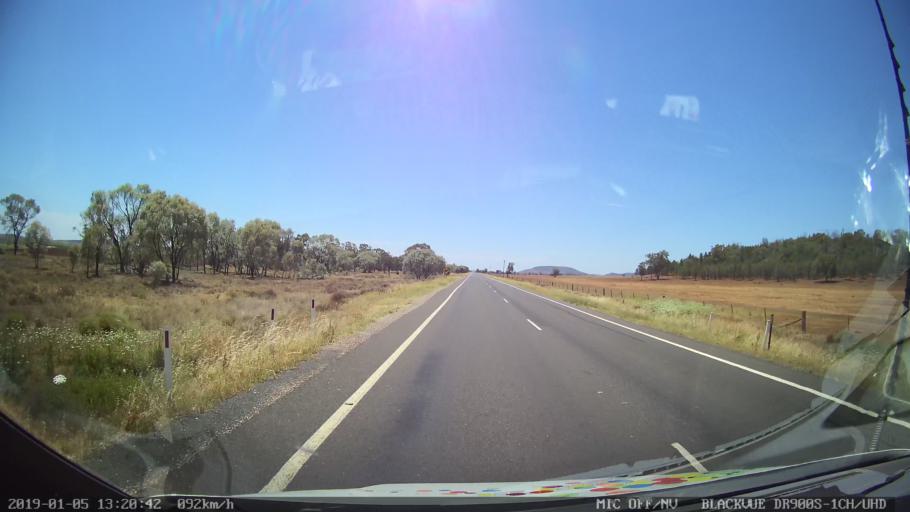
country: AU
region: New South Wales
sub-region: Gunnedah
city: Gunnedah
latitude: -31.1003
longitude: 149.9391
